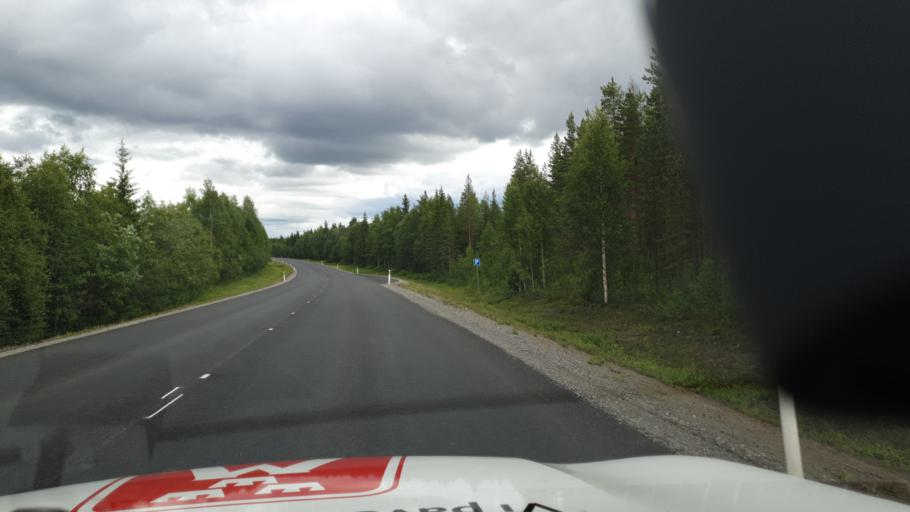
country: SE
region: Vaesterbotten
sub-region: Skelleftea Kommun
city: Langsele
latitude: 64.8865
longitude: 20.1928
